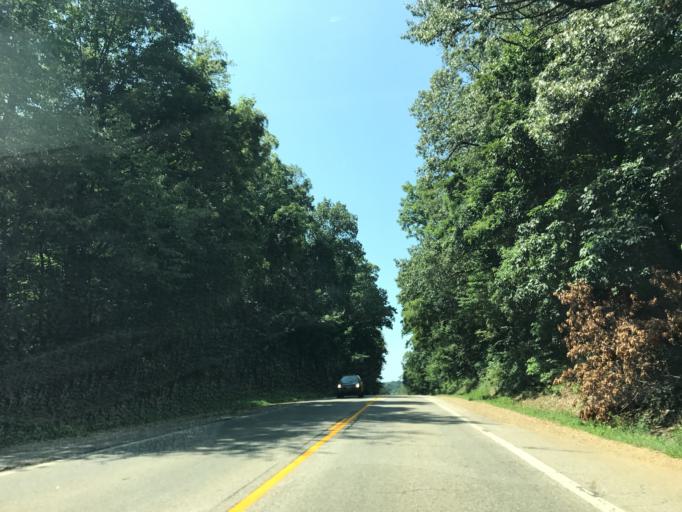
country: US
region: Michigan
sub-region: Berrien County
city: Buchanan
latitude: 41.8052
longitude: -86.3814
